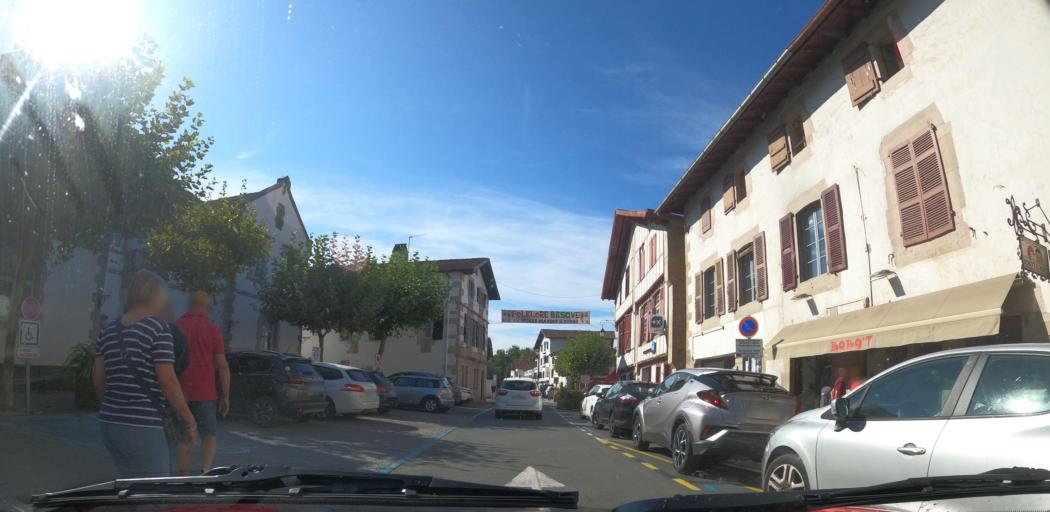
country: FR
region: Aquitaine
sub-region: Departement des Pyrenees-Atlantiques
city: Saint-Pee-sur-Nivelle
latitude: 43.3557
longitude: -1.5506
